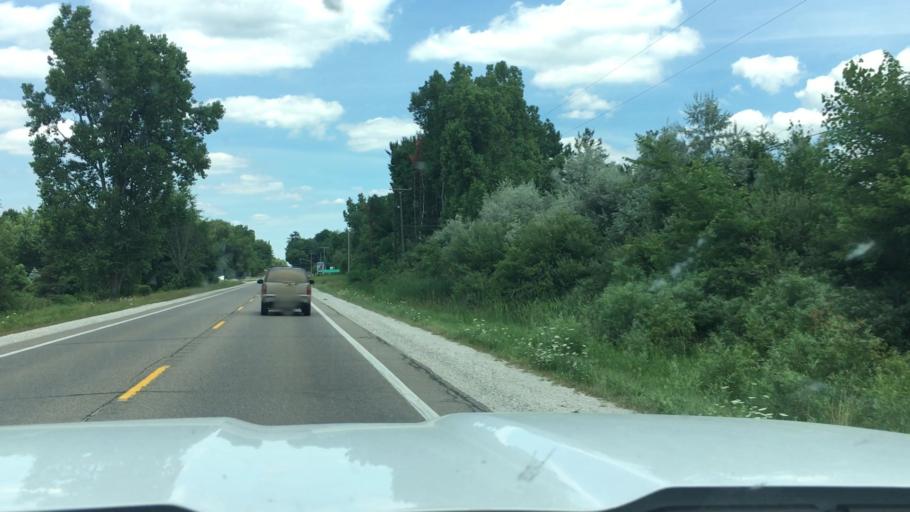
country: US
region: Michigan
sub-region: Lapeer County
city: Barnes Lake-Millers Lake
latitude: 43.1276
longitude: -83.3101
